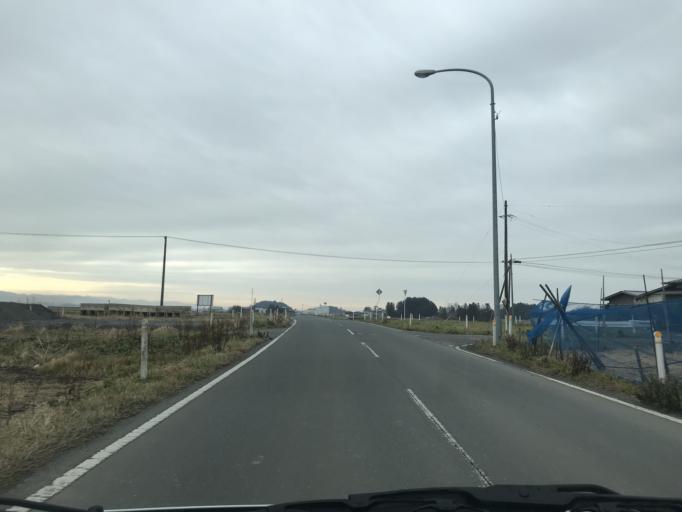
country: JP
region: Iwate
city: Ichinoseki
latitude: 38.7451
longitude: 141.2247
